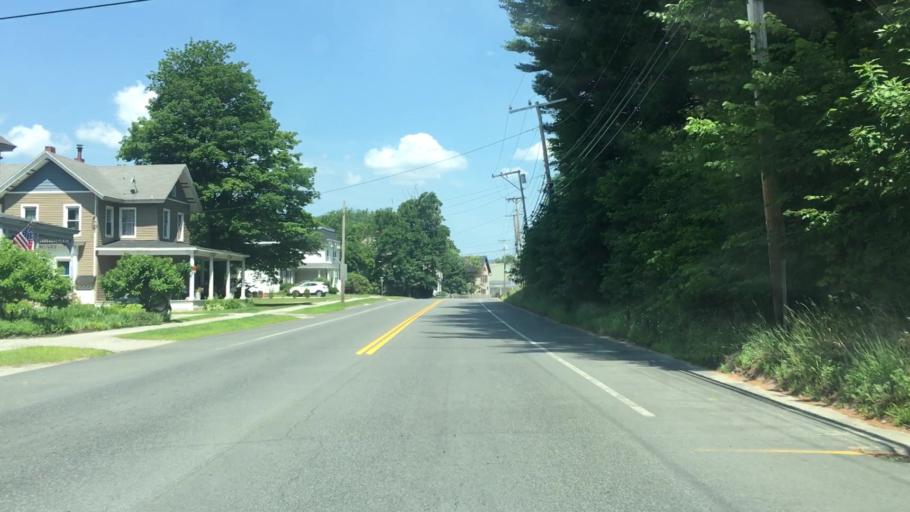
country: US
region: New Hampshire
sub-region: Sullivan County
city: Newport
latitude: 43.3682
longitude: -72.1764
